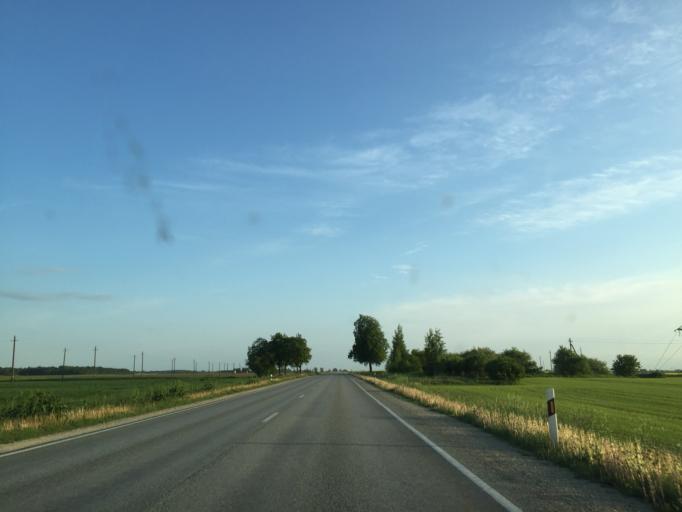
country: LT
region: Siauliu apskritis
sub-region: Joniskis
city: Joniskis
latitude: 56.1075
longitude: 23.4862
